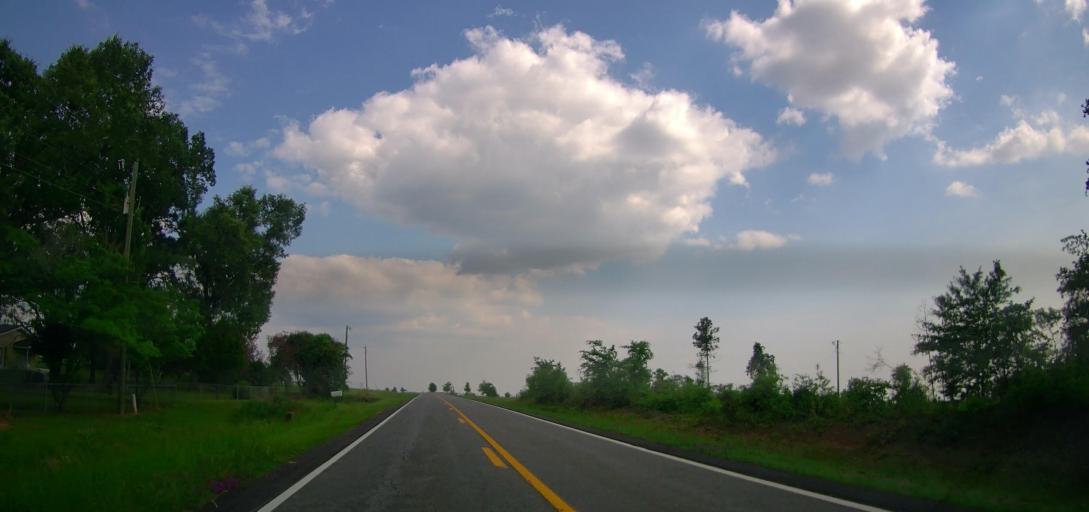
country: US
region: Georgia
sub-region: Laurens County
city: East Dublin
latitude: 32.6283
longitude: -82.8877
